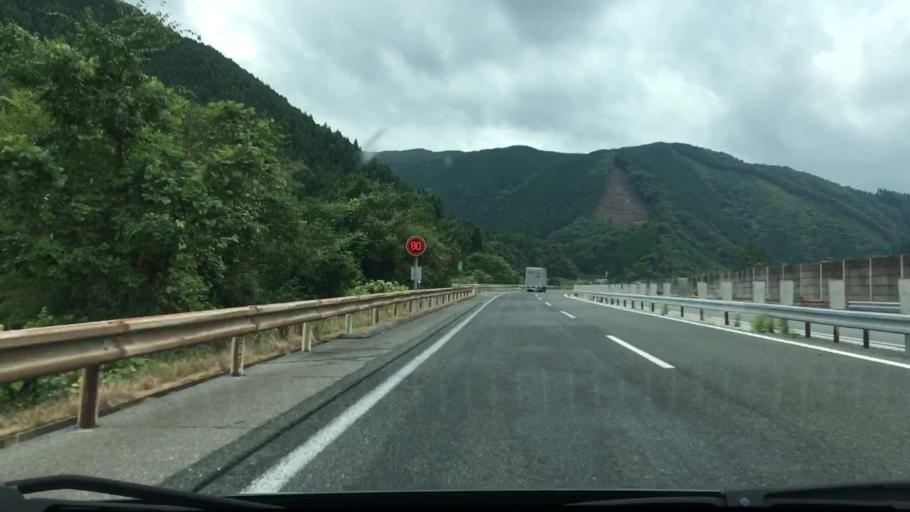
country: JP
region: Okayama
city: Niimi
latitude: 34.9763
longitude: 133.3722
